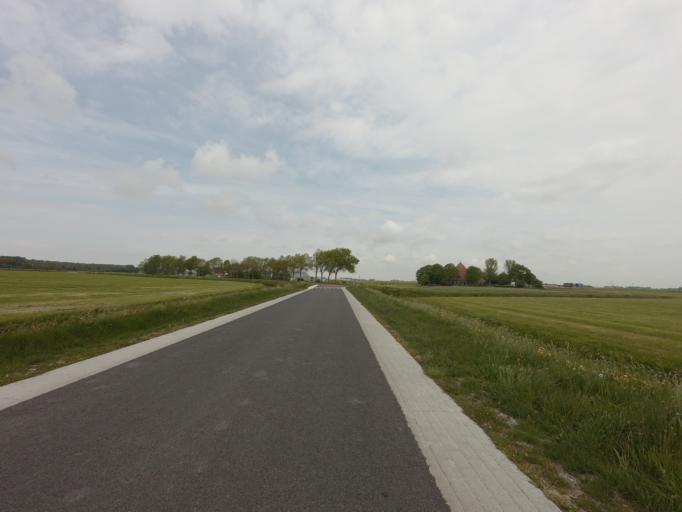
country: NL
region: Friesland
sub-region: Sudwest Fryslan
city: Bolsward
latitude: 53.0867
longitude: 5.4832
